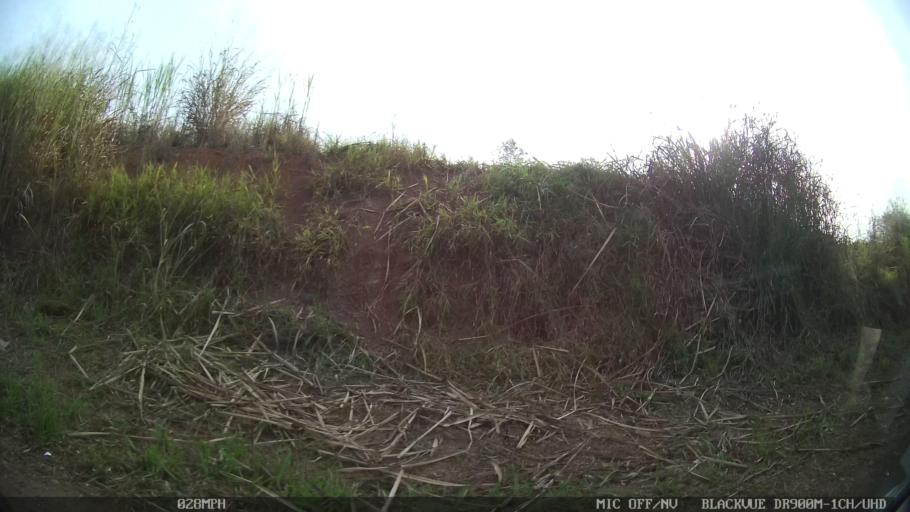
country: BR
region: Sao Paulo
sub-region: Piracicaba
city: Piracicaba
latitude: -22.7023
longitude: -47.5879
